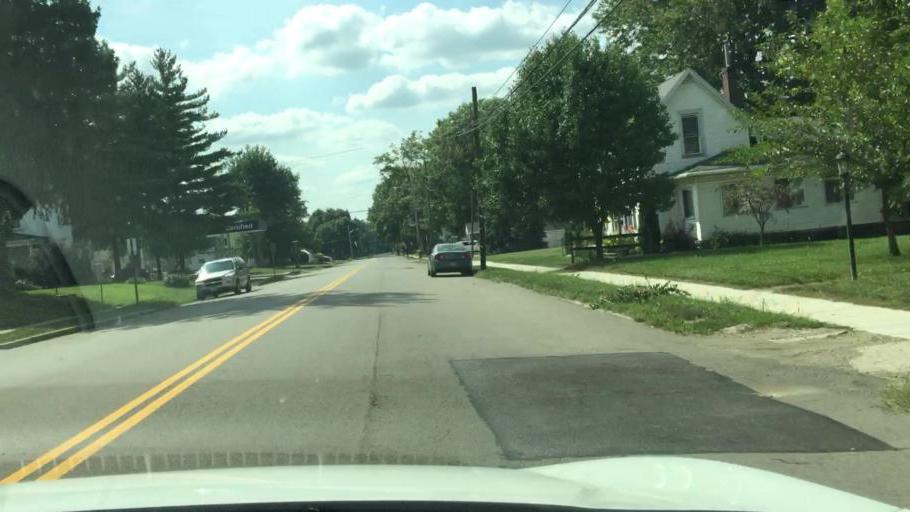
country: US
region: Ohio
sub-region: Champaign County
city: Mechanicsburg
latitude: 40.0751
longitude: -83.5621
